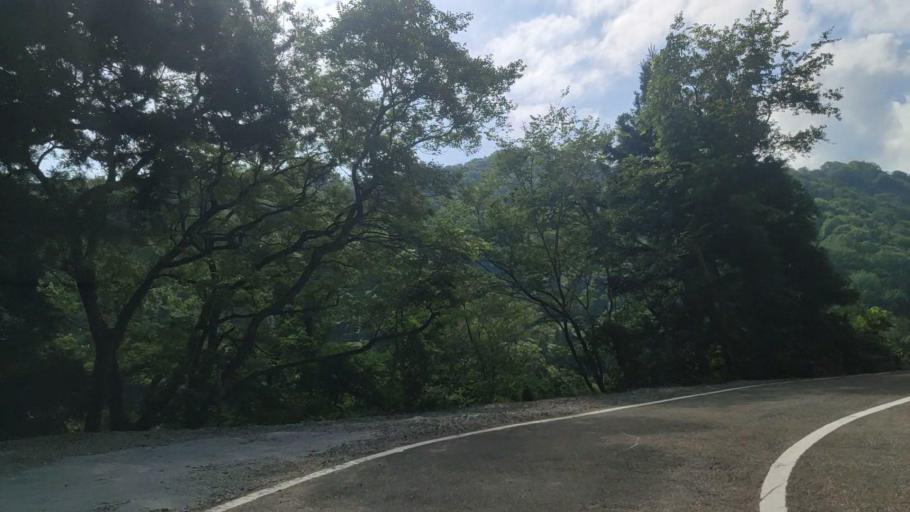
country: JP
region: Ishikawa
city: Komatsu
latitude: 36.2923
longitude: 136.5288
